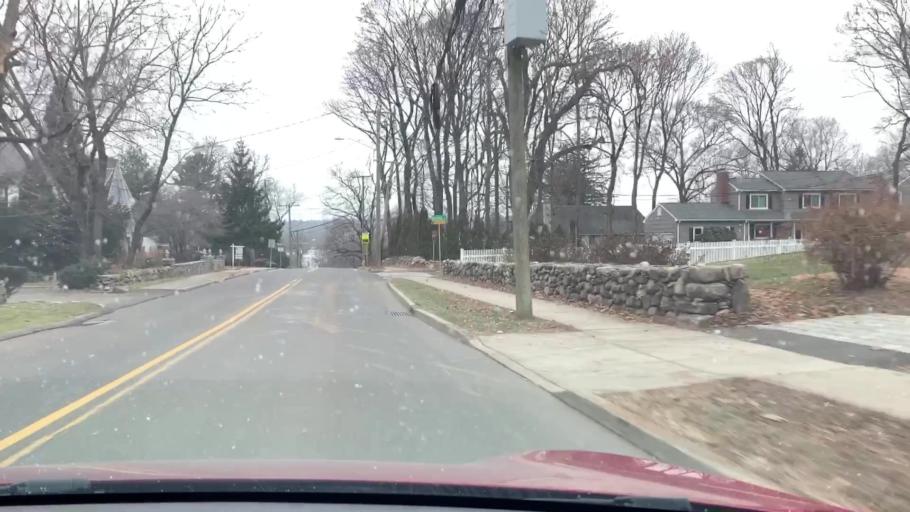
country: US
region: Connecticut
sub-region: Fairfield County
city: Stamford
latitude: 41.0674
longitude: -73.5370
